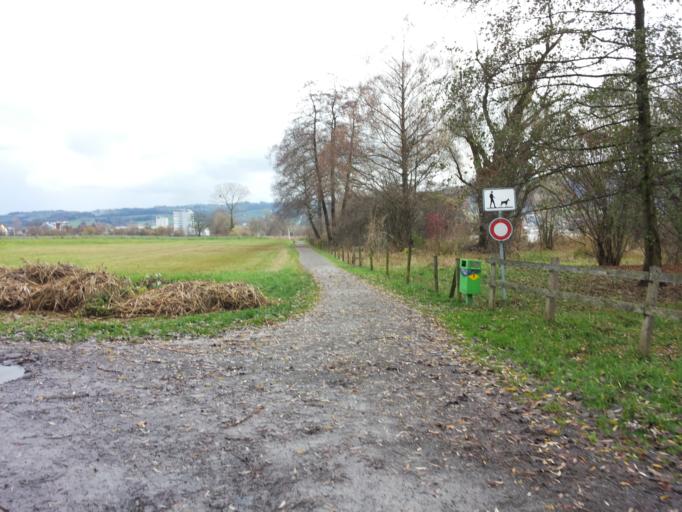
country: CH
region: Zug
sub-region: Zug
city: Steinhausen
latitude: 47.1780
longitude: 8.4827
